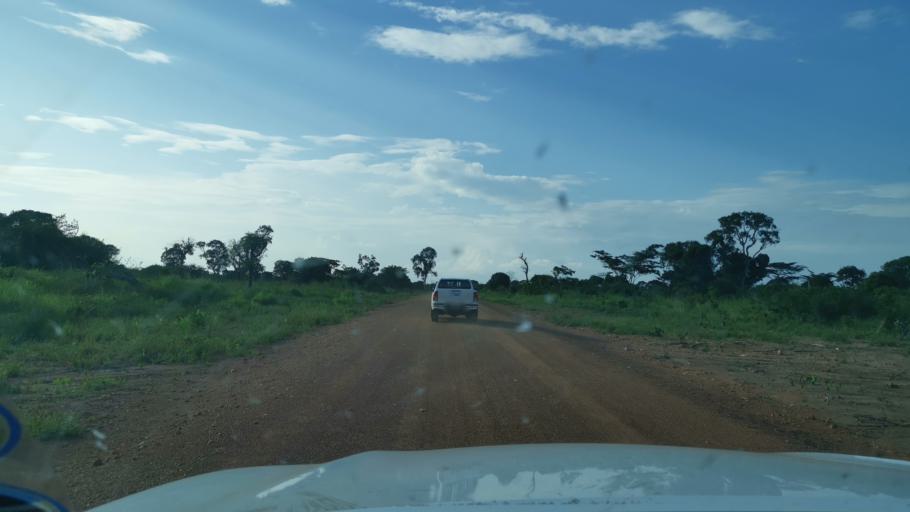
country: ZM
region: Luapula
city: Samfya
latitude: -11.1184
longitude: 29.5796
